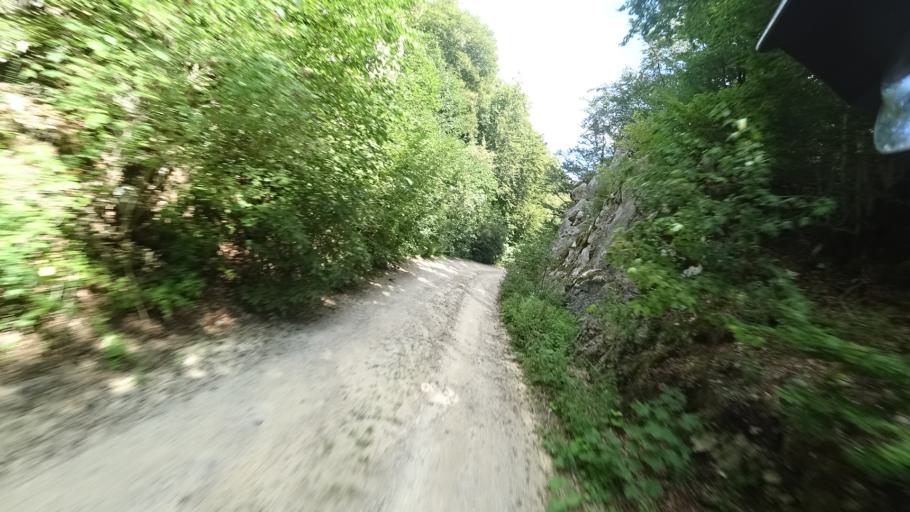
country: BA
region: Federation of Bosnia and Herzegovina
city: Orasac
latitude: 44.5691
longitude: 15.8438
